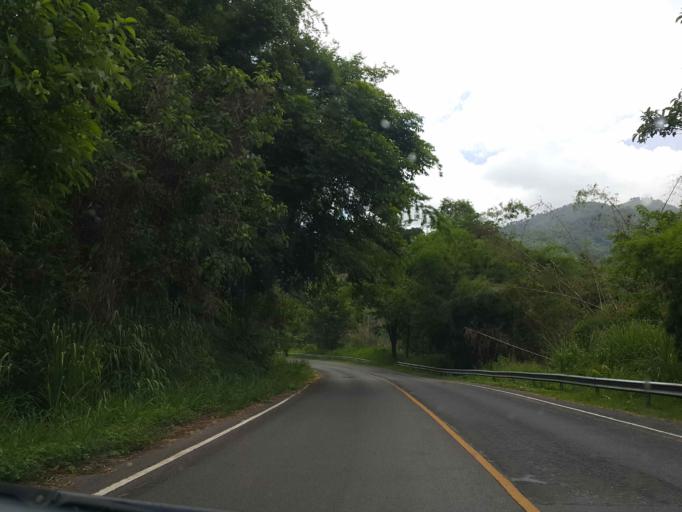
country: TH
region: Chiang Mai
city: Samoeng
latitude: 18.8252
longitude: 98.7836
